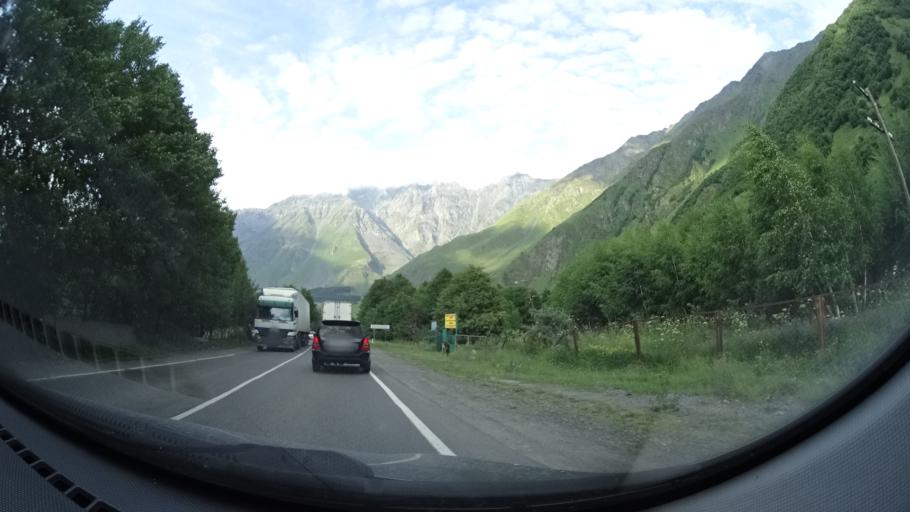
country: GE
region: Mtskheta-Mtianeti
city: Step'antsminda
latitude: 42.6429
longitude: 44.6379
